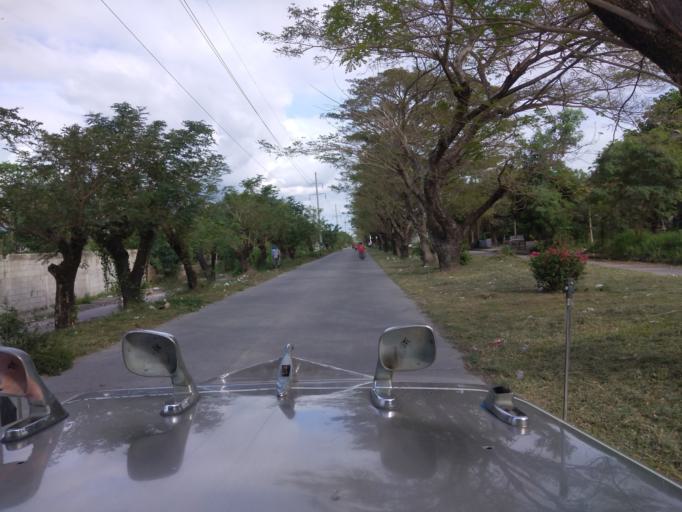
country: PH
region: Central Luzon
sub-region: Province of Pampanga
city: Pandacaqui
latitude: 15.1777
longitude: 120.6593
